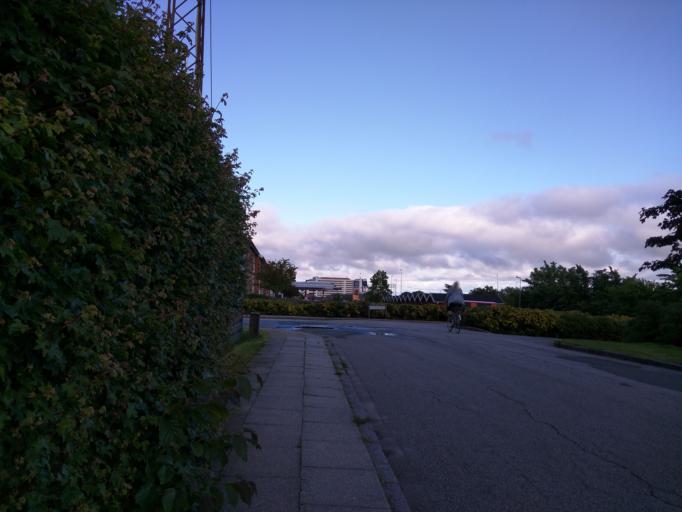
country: DK
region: Central Jutland
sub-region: Viborg Kommune
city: Viborg
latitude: 56.4508
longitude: 9.3893
